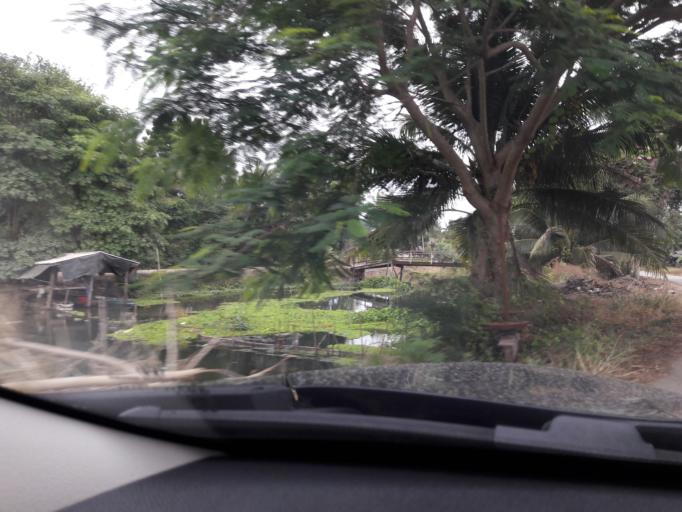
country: TH
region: Ratchaburi
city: Damnoen Saduak
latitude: 13.6038
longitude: 99.9732
